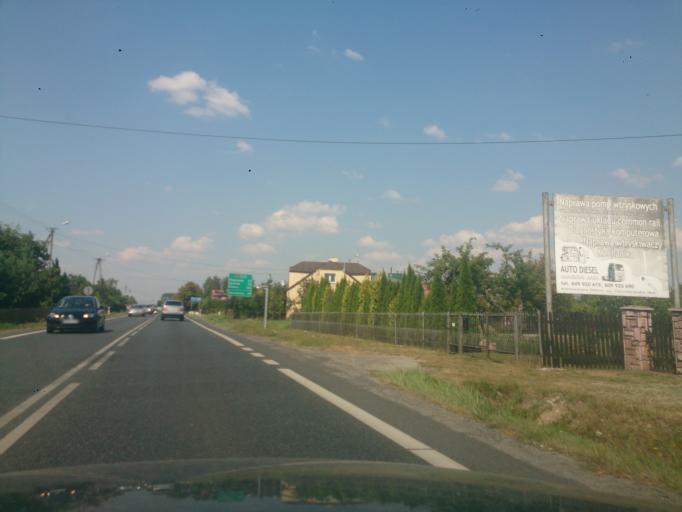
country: PL
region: Subcarpathian Voivodeship
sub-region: Powiat kolbuszowski
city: Kolbuszowa
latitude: 50.2539
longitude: 21.7714
